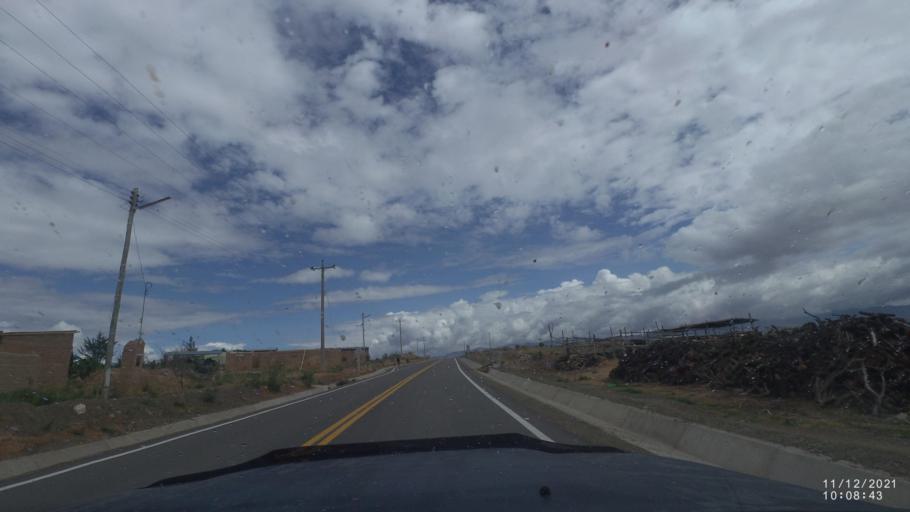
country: BO
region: Cochabamba
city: Tarata
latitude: -17.6641
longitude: -65.9649
